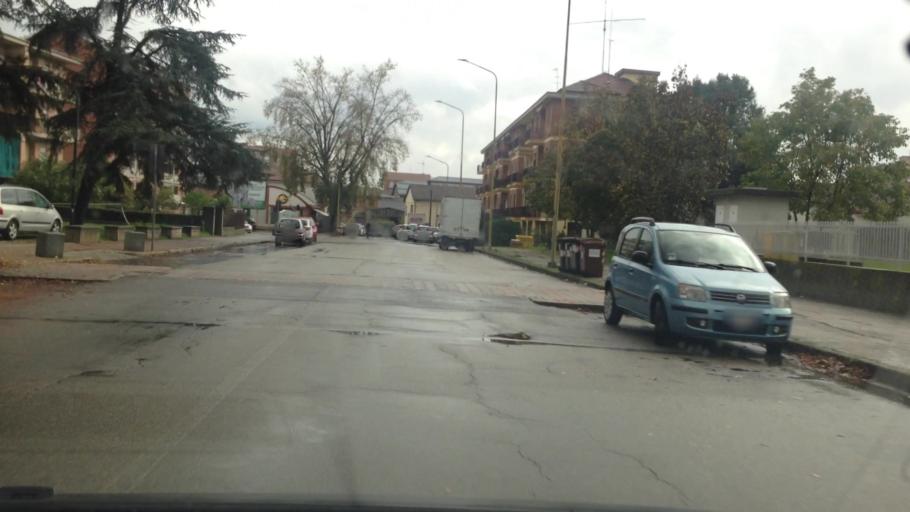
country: IT
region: Piedmont
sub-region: Provincia di Asti
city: Asti
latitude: 44.9081
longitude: 8.2201
